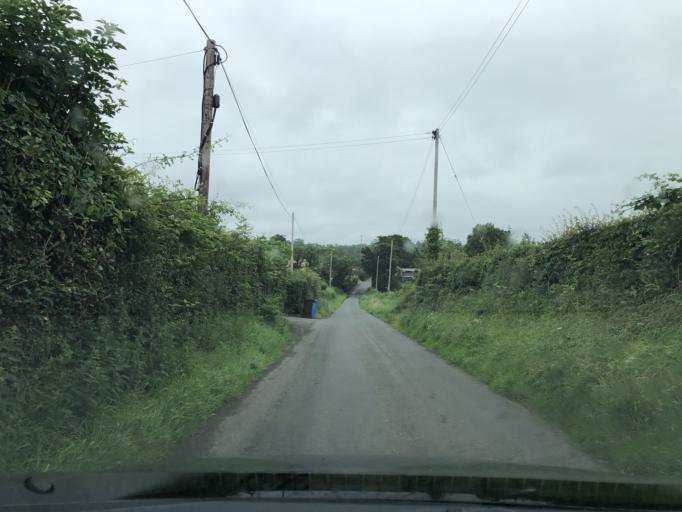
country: GB
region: Northern Ireland
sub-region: Down District
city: Dundrum
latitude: 54.3023
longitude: -5.8523
